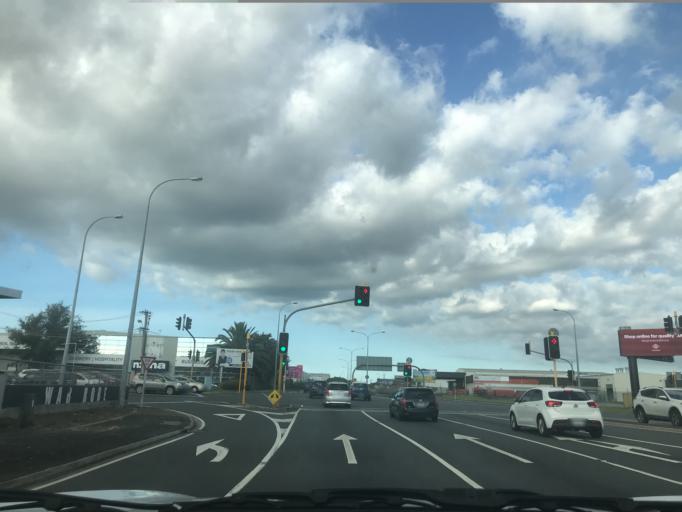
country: NZ
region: Auckland
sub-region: Auckland
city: Tamaki
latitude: -36.9153
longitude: 174.8457
